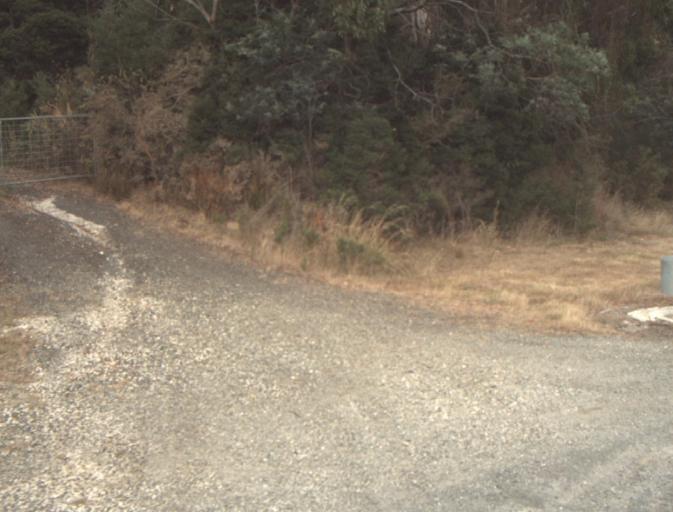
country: AU
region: Tasmania
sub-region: Launceston
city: Mayfield
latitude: -41.2659
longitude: 147.2150
